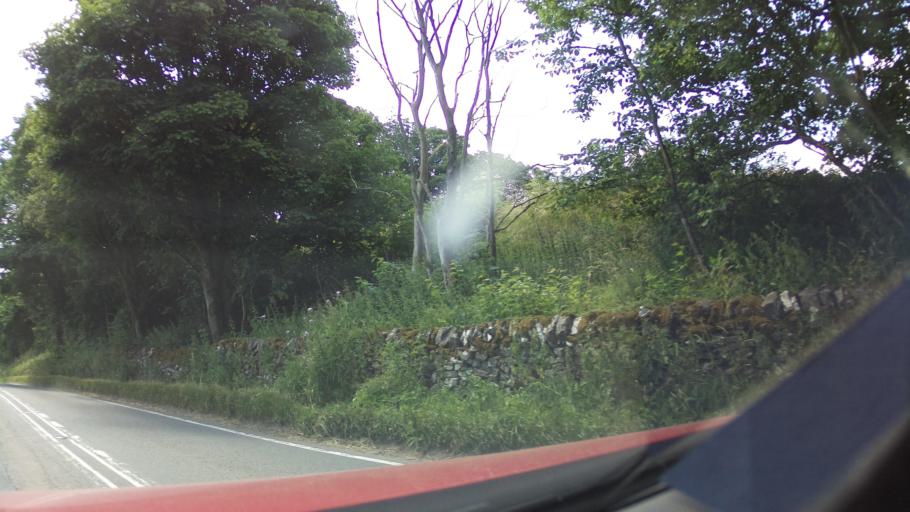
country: GB
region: England
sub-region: Derbyshire
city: Ashbourne
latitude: 53.0975
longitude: -1.7727
